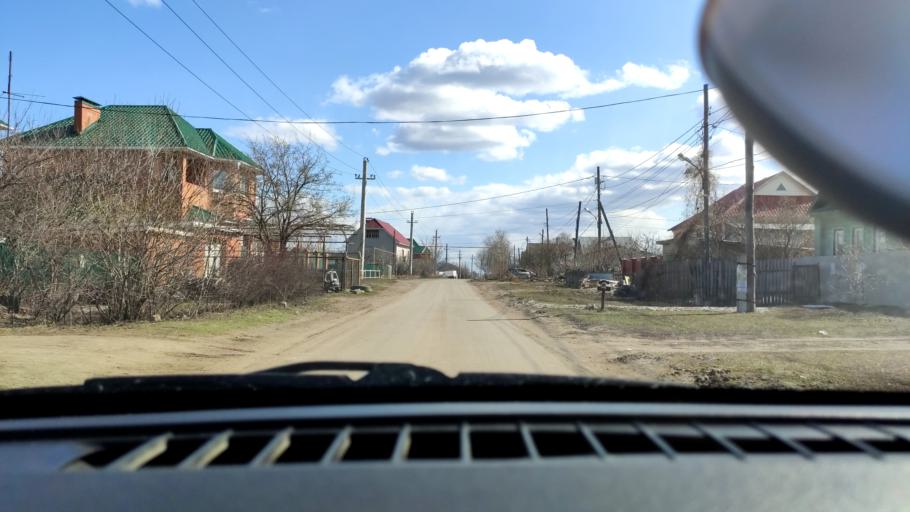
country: RU
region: Samara
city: Petra-Dubrava
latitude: 53.2934
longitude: 50.3099
